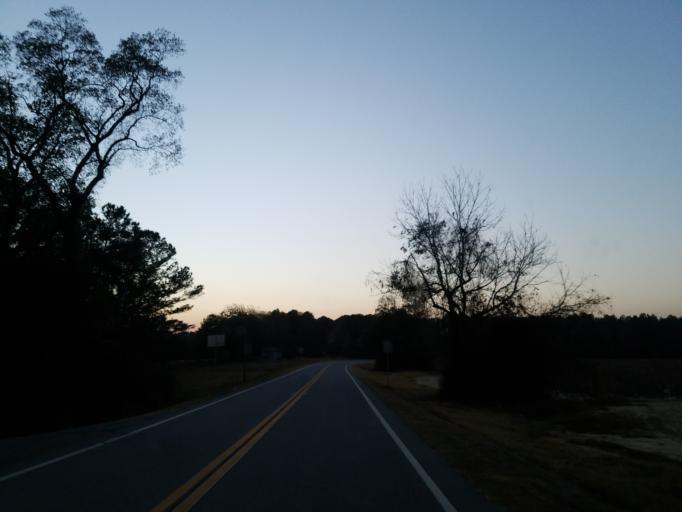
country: US
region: Georgia
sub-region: Wilcox County
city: Rochelle
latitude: 31.8104
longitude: -83.4934
